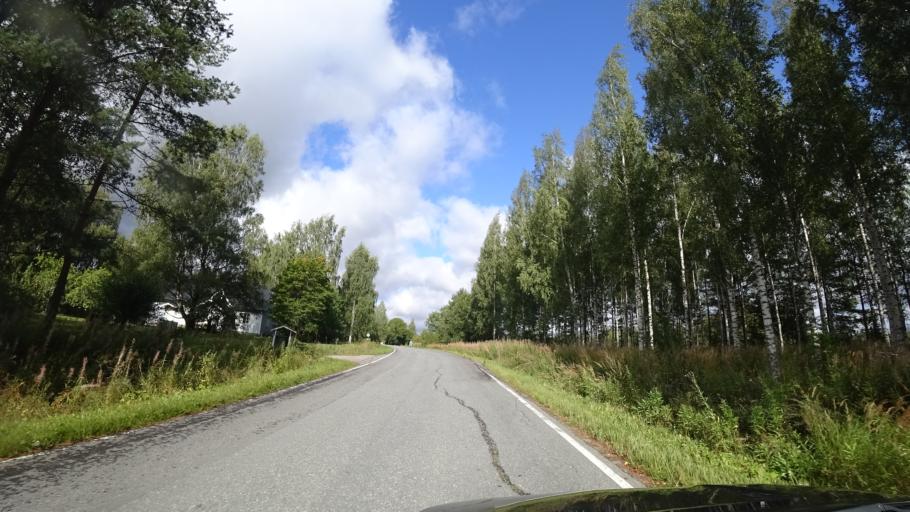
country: FI
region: Haeme
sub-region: Riihimaeki
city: Hausjaervi
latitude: 60.7154
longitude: 24.9705
